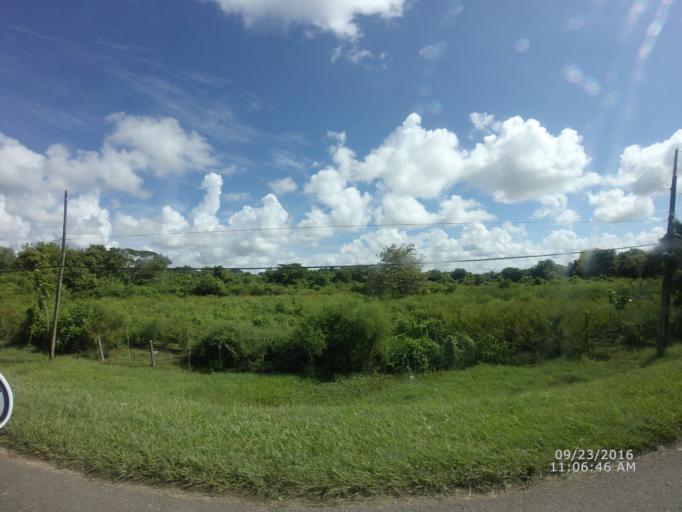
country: CU
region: Mayabeque
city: Jamaica
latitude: 23.0125
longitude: -82.2244
